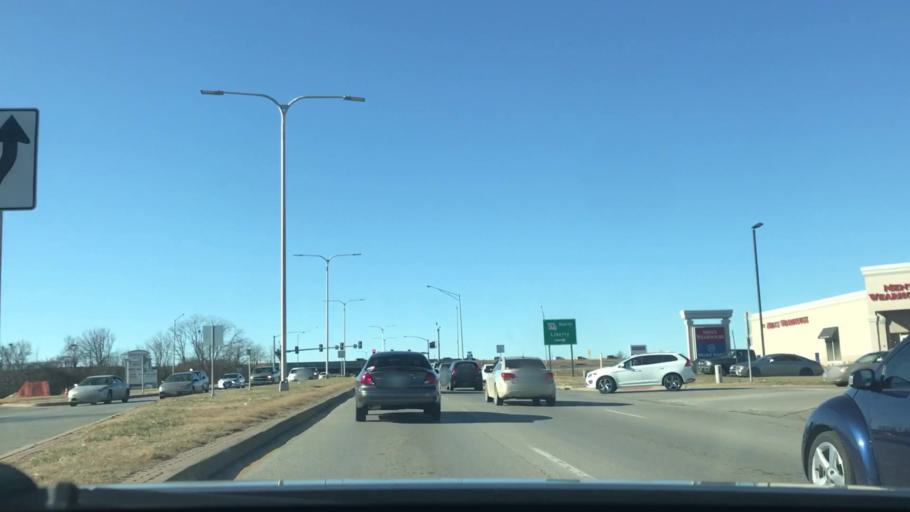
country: US
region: Missouri
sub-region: Jackson County
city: East Independence
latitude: 39.0481
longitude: -94.3607
